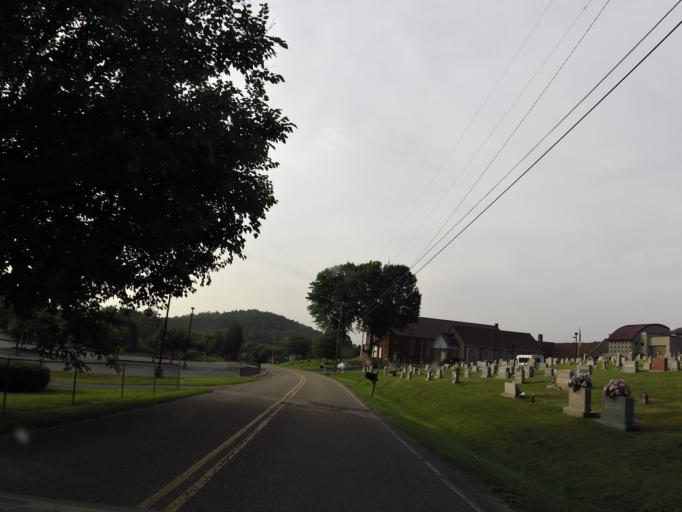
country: US
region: Tennessee
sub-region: Sevier County
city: Seymour
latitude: 35.8913
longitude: -83.7954
